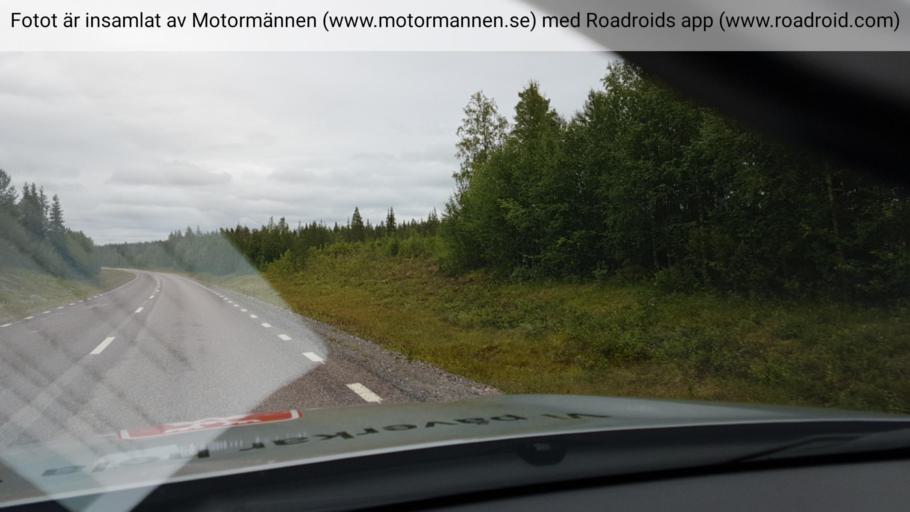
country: SE
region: Norrbotten
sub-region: Gallivare Kommun
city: Gaellivare
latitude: 67.0698
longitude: 21.4963
